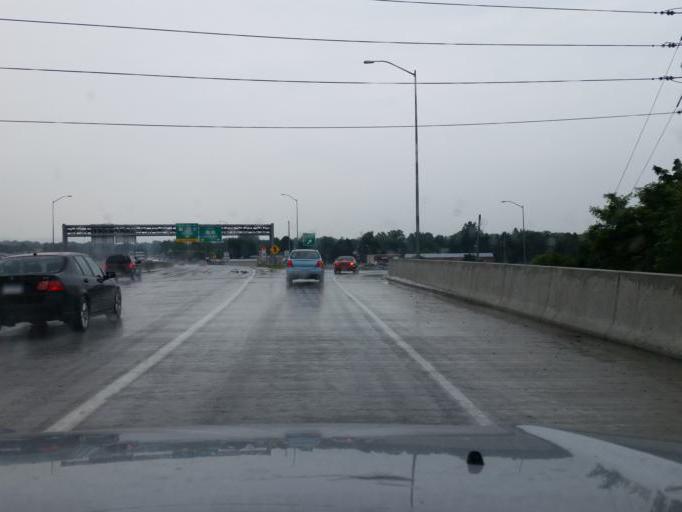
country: US
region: Pennsylvania
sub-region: Cumberland County
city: Camp Hill
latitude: 40.2297
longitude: -76.9321
